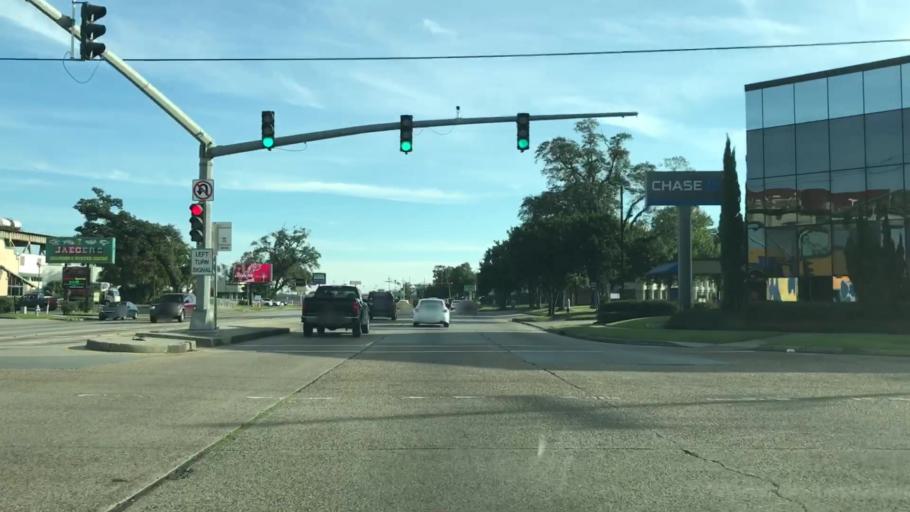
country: US
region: Louisiana
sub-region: Jefferson Parish
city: Elmwood
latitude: 29.9584
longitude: -90.1833
